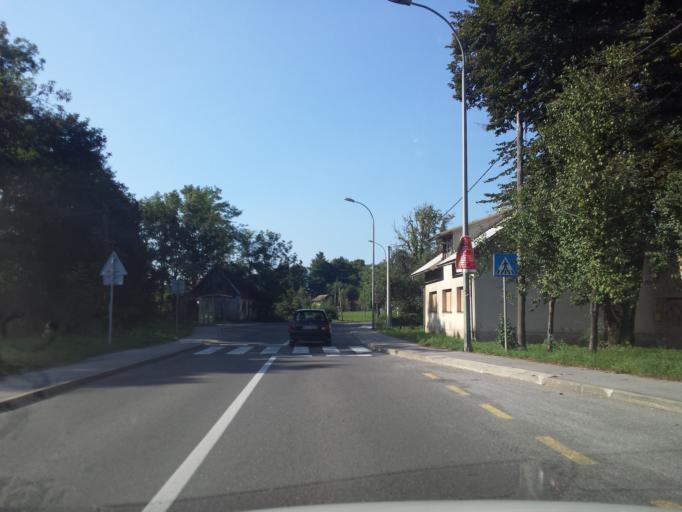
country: HR
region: Karlovacka
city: Ostarije
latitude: 45.2368
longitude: 15.2535
